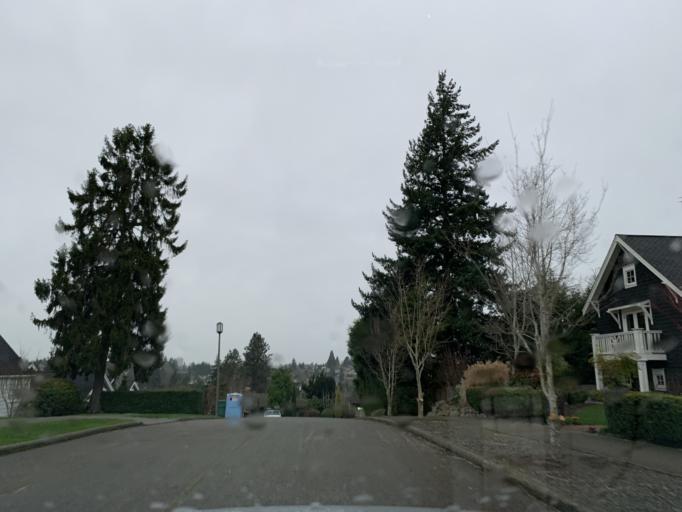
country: US
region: Washington
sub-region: King County
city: Yarrow Point
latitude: 47.6700
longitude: -122.2623
